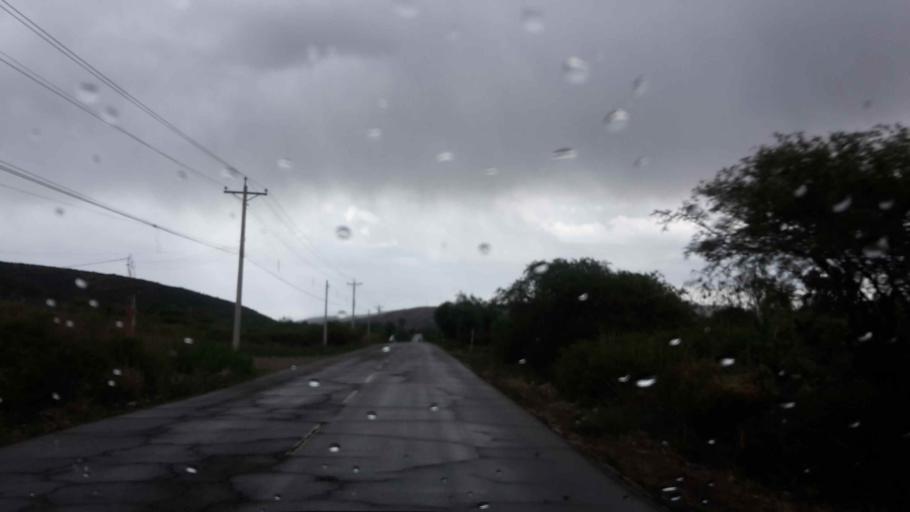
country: BO
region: Cochabamba
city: Tarata
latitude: -17.5714
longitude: -66.0683
